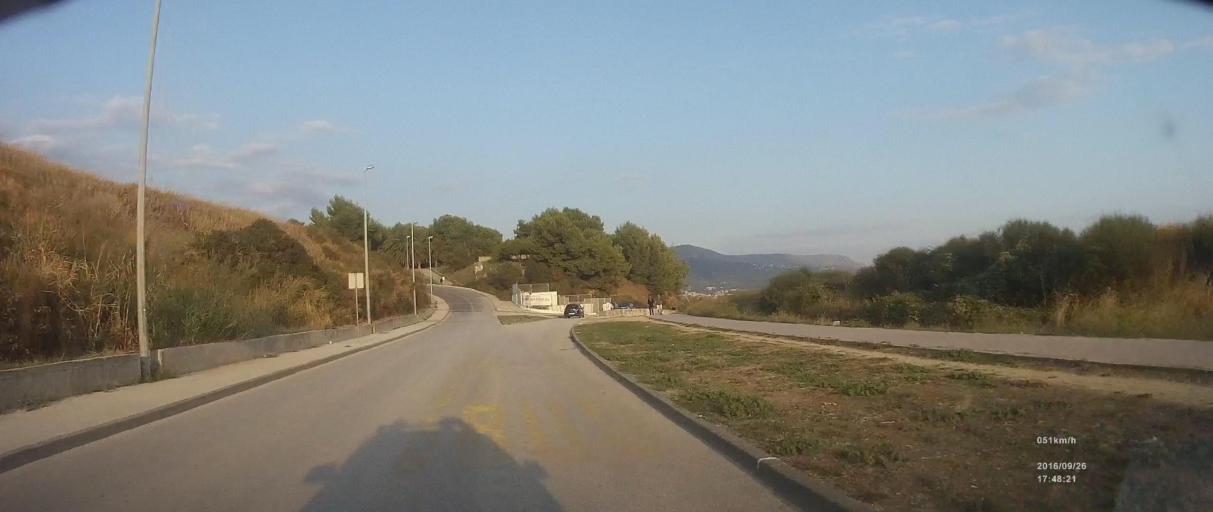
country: HR
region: Splitsko-Dalmatinska
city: Kamen
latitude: 43.5019
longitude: 16.4911
